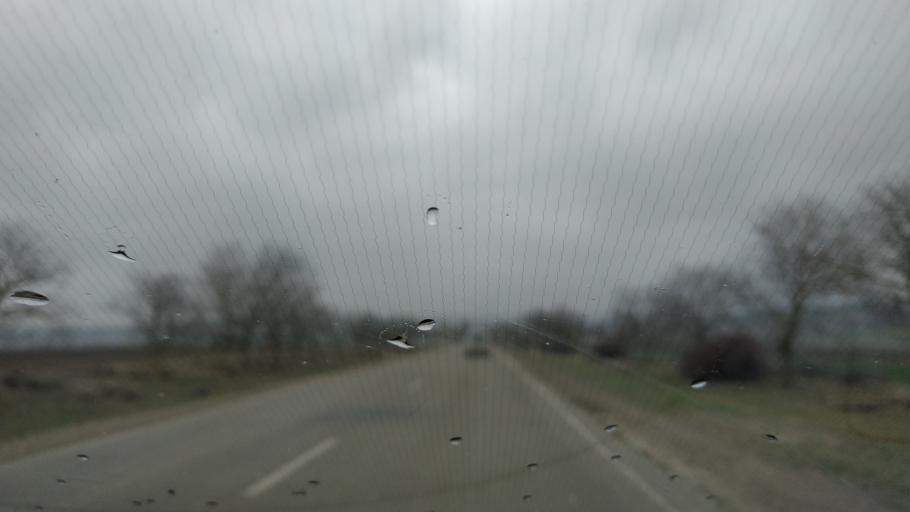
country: MD
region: Gagauzia
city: Comrat
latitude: 46.2496
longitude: 28.7590
